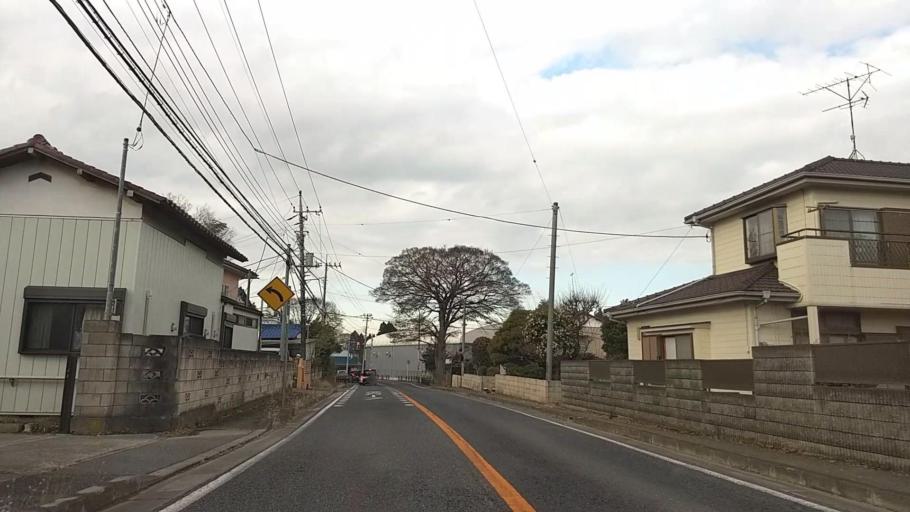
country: JP
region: Chiba
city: Oami
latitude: 35.5779
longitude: 140.2669
